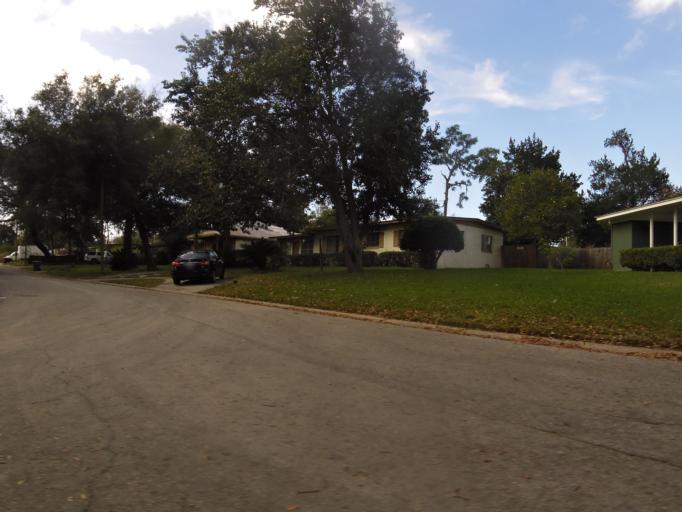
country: US
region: Florida
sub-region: Duval County
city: Jacksonville
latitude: 30.3412
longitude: -81.5825
